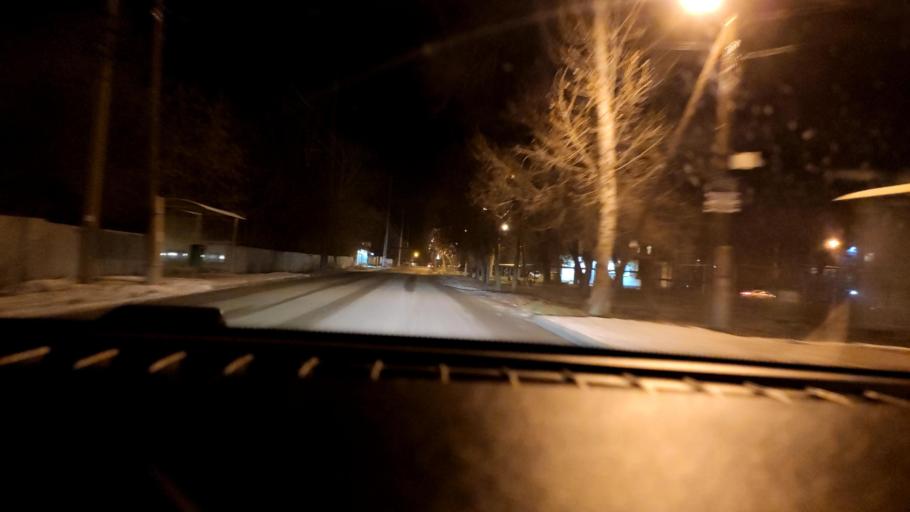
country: RU
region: Samara
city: Samara
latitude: 53.1369
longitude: 50.1551
